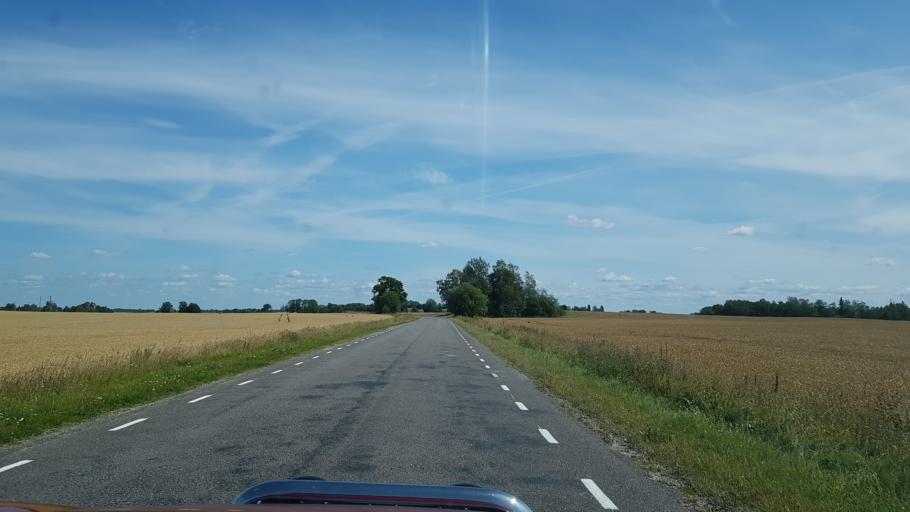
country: EE
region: Jaervamaa
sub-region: Koeru vald
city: Koeru
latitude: 59.0413
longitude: 25.9943
